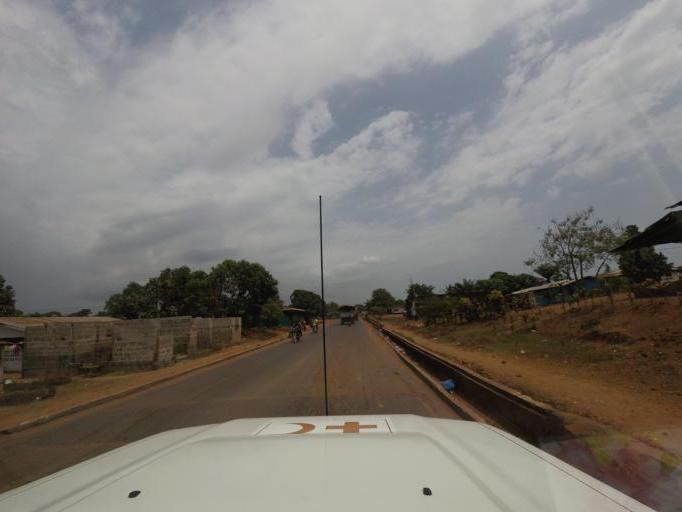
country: LR
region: Montserrado
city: Monrovia
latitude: 6.3081
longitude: -10.6971
